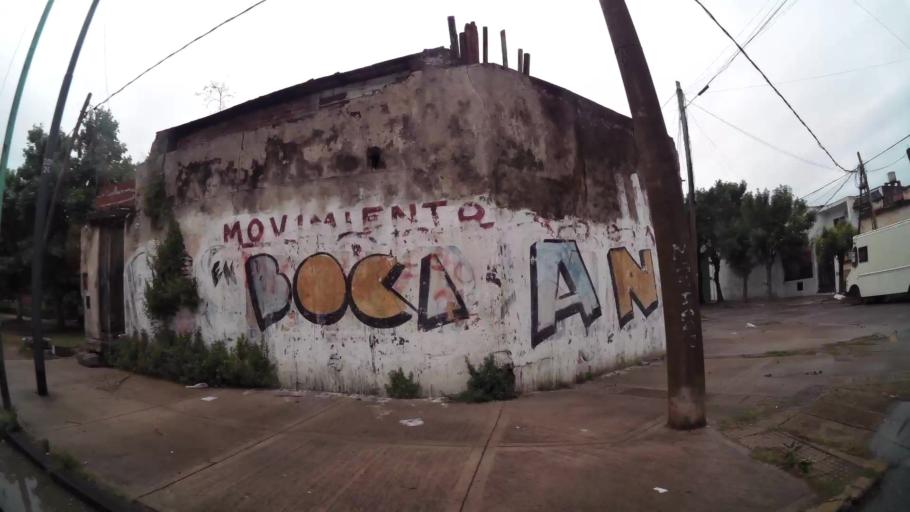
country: AR
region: Buenos Aires F.D.
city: Villa Lugano
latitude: -34.6579
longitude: -58.4450
